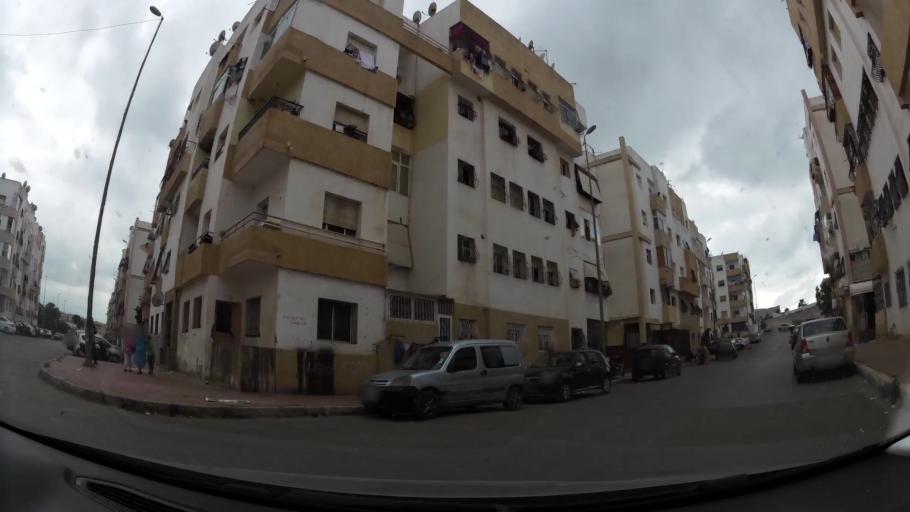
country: MA
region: Rabat-Sale-Zemmour-Zaer
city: Sale
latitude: 34.0405
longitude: -6.7985
